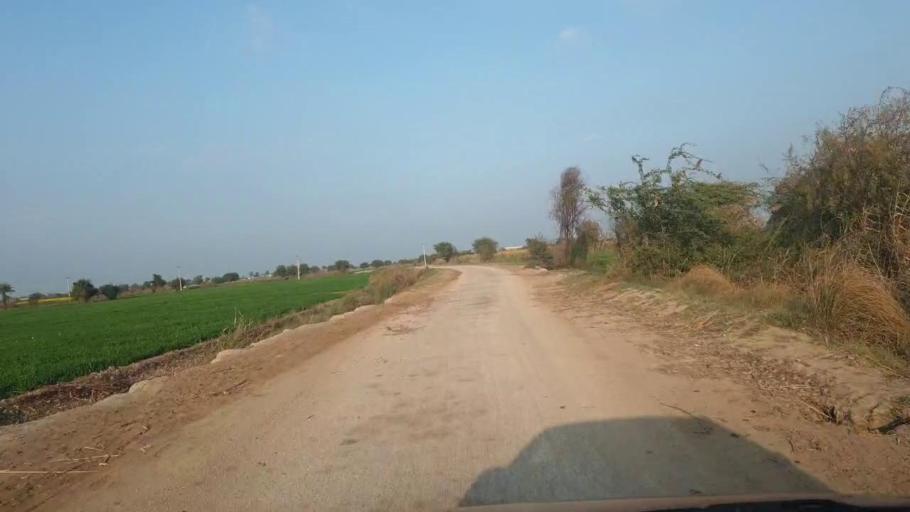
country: PK
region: Sindh
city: Berani
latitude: 25.8566
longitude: 68.7357
